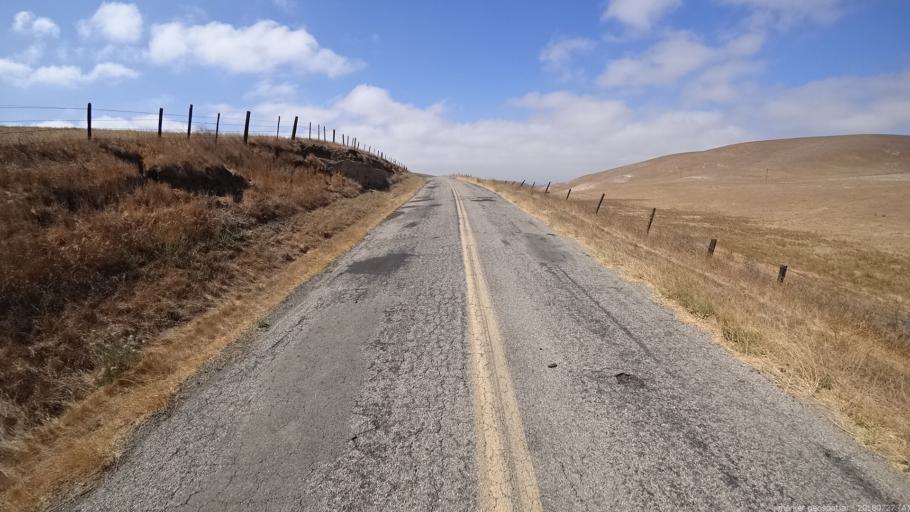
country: US
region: California
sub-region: Monterey County
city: King City
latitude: 36.2421
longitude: -121.0396
